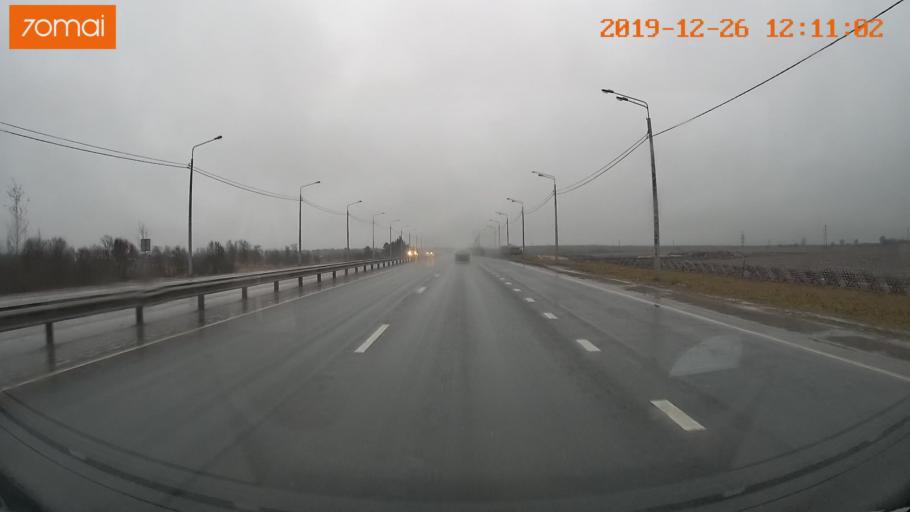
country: RU
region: Vologda
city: Tonshalovo
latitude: 59.2527
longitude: 37.9746
